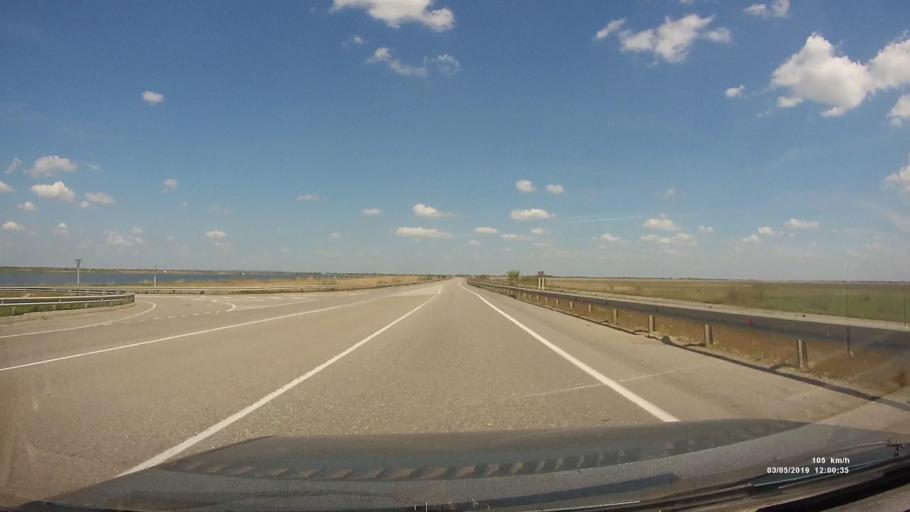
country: RU
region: Rostov
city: Bagayevskaya
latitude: 47.2508
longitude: 40.3417
